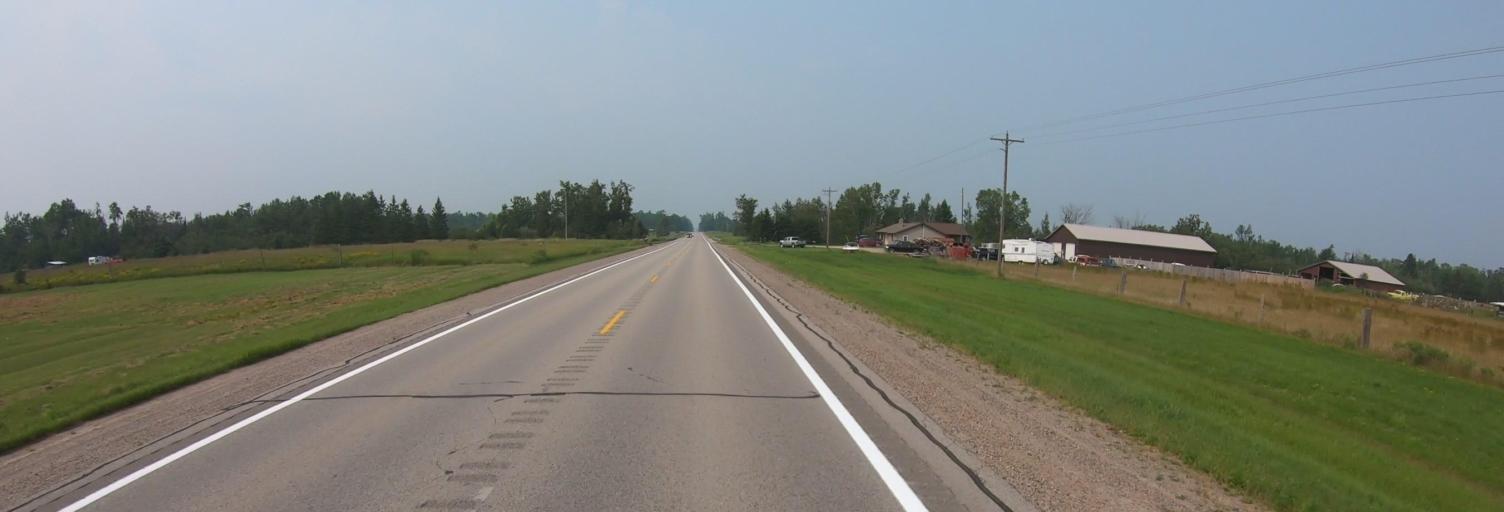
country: US
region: Michigan
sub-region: Chippewa County
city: Sault Ste. Marie
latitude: 46.2323
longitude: -84.3634
